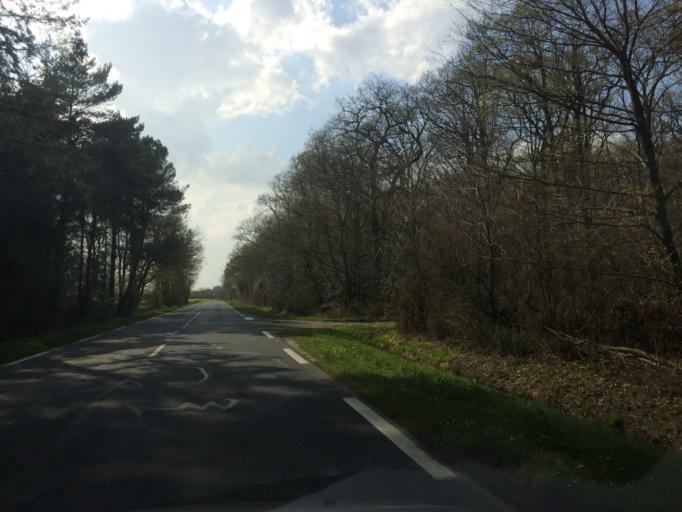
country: FR
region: Pays de la Loire
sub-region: Departement de la Loire-Atlantique
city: Bouvron
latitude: 47.4853
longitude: -1.8383
